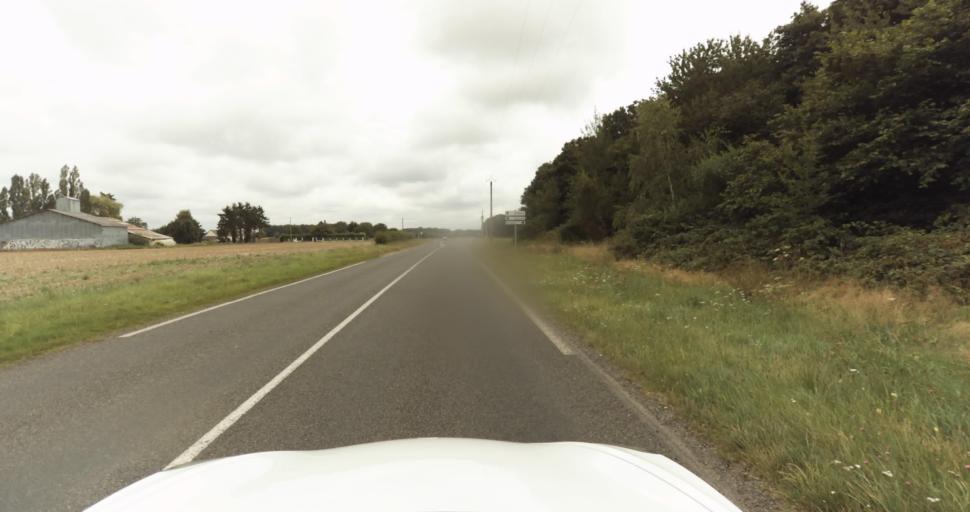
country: FR
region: Haute-Normandie
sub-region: Departement de l'Eure
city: Saint-Sebastien-de-Morsent
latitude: 49.0341
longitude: 1.0630
